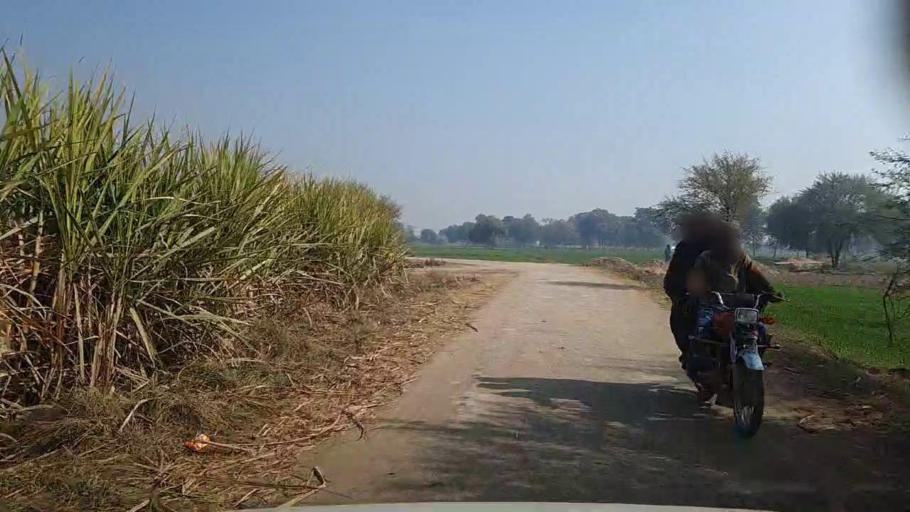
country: PK
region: Sindh
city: Khairpur
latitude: 27.9424
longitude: 69.6658
